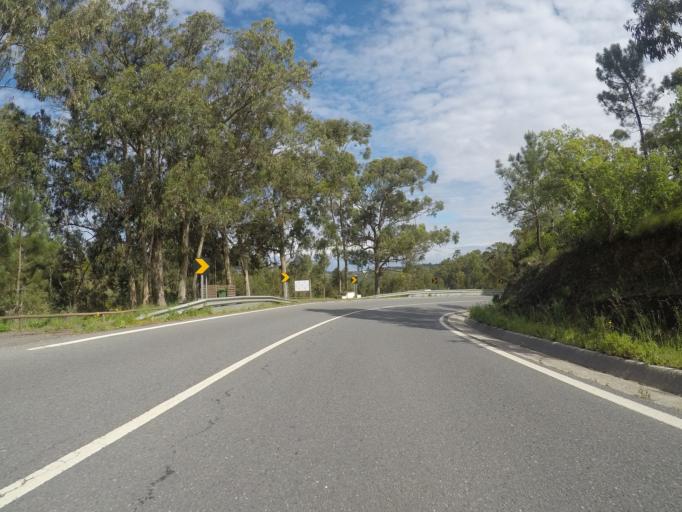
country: PT
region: Beja
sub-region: Odemira
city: Sao Teotonio
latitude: 37.4264
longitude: -8.7661
